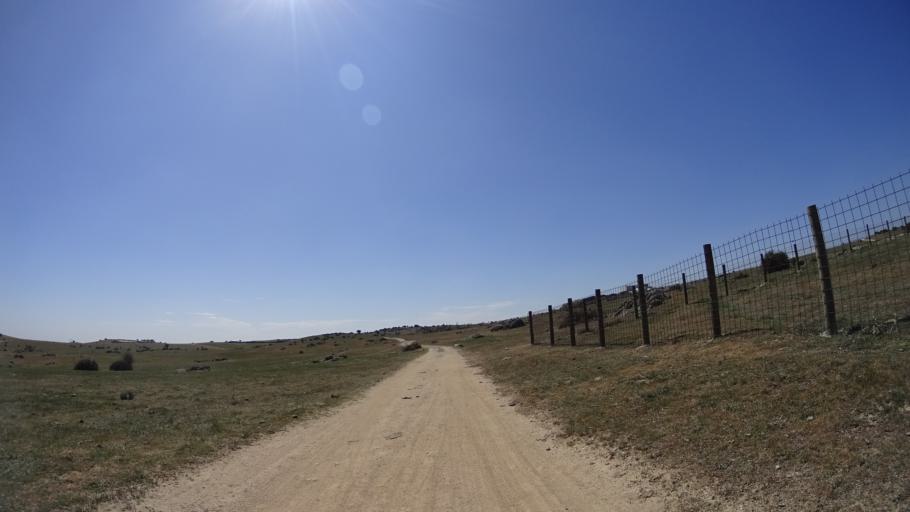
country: ES
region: Madrid
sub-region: Provincia de Madrid
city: Colmenar Viejo
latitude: 40.6985
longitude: -3.7550
